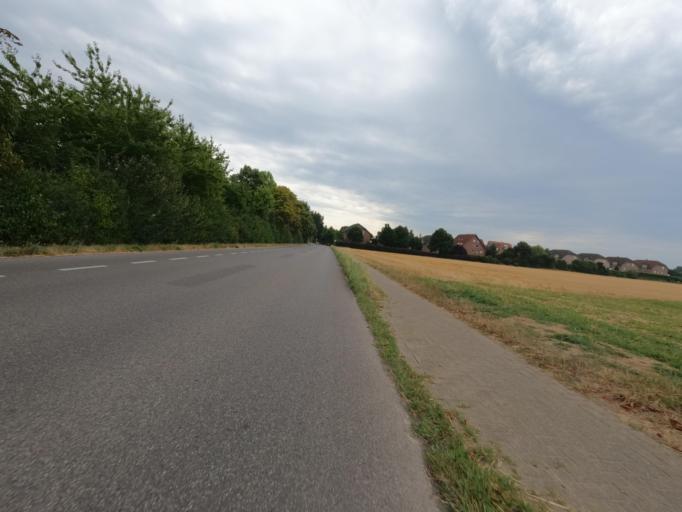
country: DE
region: North Rhine-Westphalia
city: Geilenkirchen
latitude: 50.9749
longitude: 6.1046
